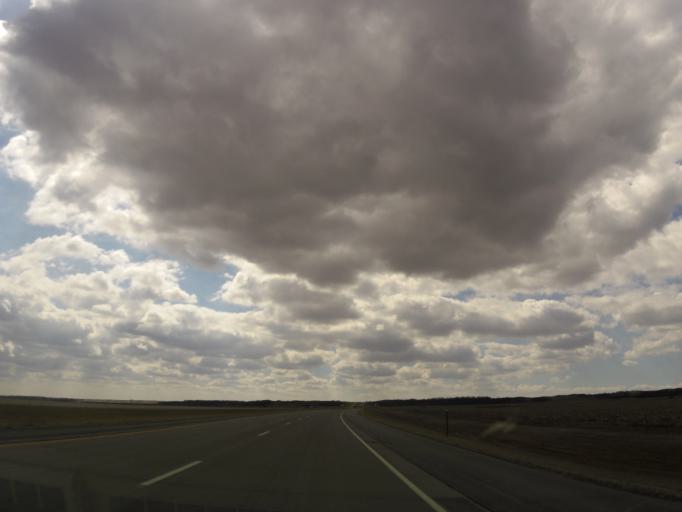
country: US
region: South Dakota
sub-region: Roberts County
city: Sisseton
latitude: 45.4403
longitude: -96.9915
